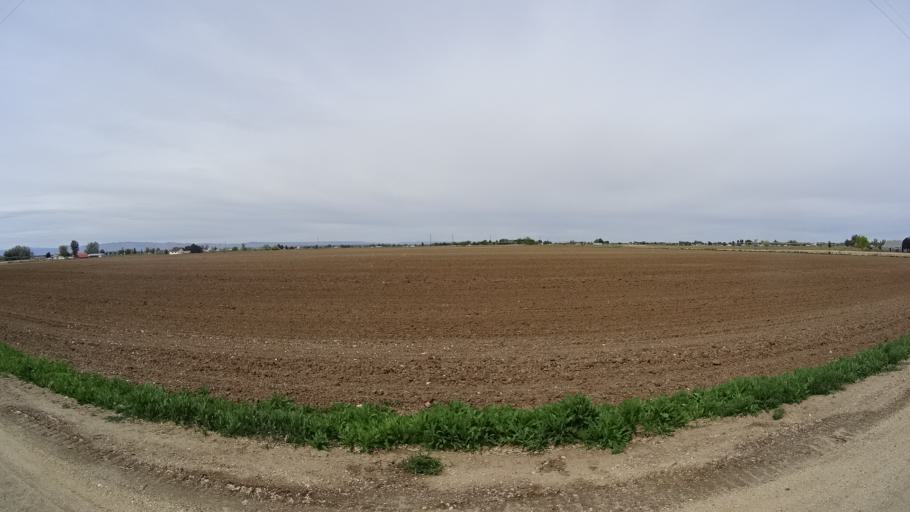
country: US
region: Idaho
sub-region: Ada County
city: Kuna
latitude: 43.5517
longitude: -116.4736
